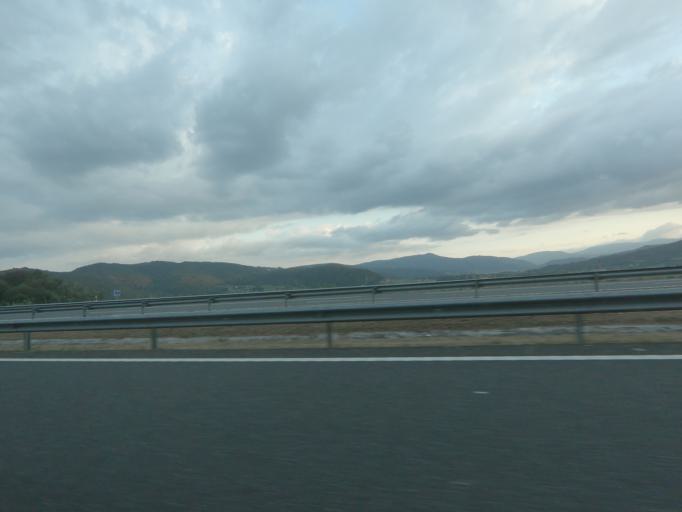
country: ES
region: Galicia
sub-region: Provincia de Ourense
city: Castrelo de Mino
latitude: 42.3348
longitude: -8.0463
